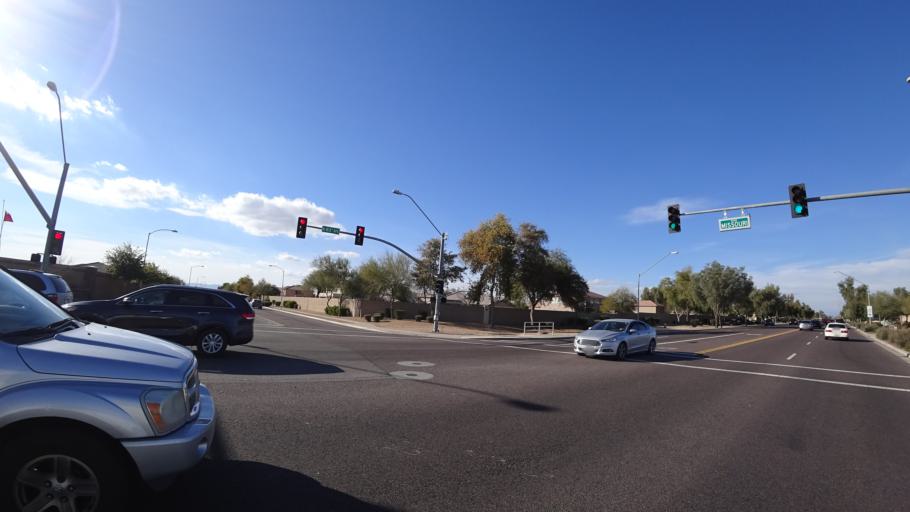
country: US
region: Arizona
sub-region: Maricopa County
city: Glendale
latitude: 33.5160
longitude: -112.2376
